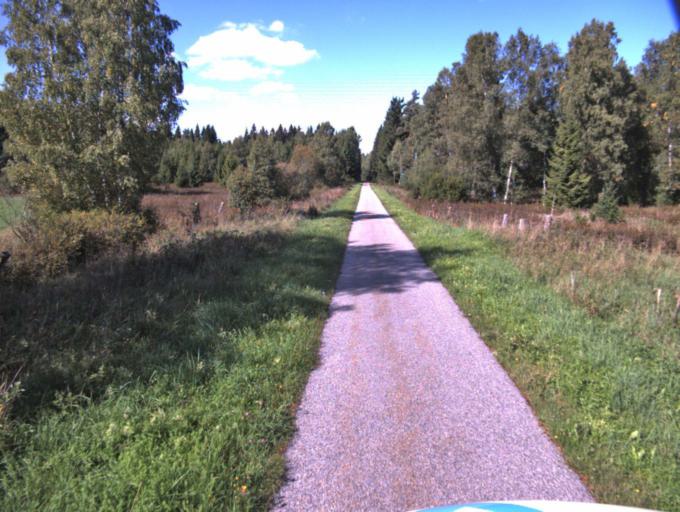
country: SE
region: Vaestra Goetaland
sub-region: Ulricehamns Kommun
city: Ulricehamn
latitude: 57.8340
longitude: 13.3395
